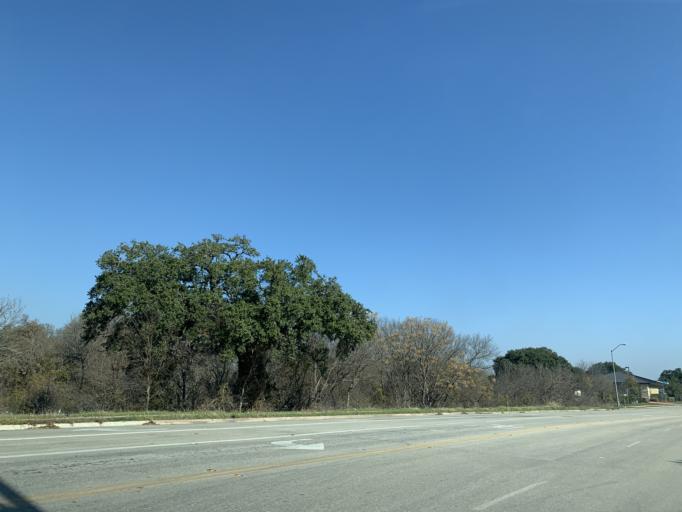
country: US
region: Texas
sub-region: Williamson County
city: Round Rock
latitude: 30.5245
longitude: -97.6409
